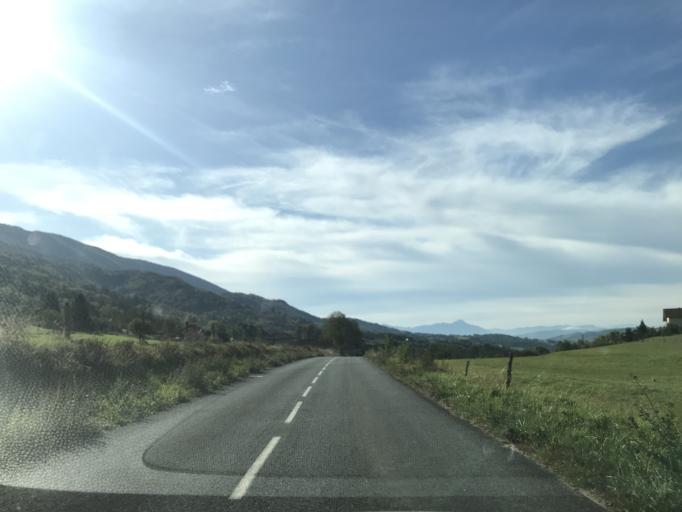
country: FR
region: Rhone-Alpes
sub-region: Departement de la Savoie
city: Yenne
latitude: 45.6583
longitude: 5.7890
